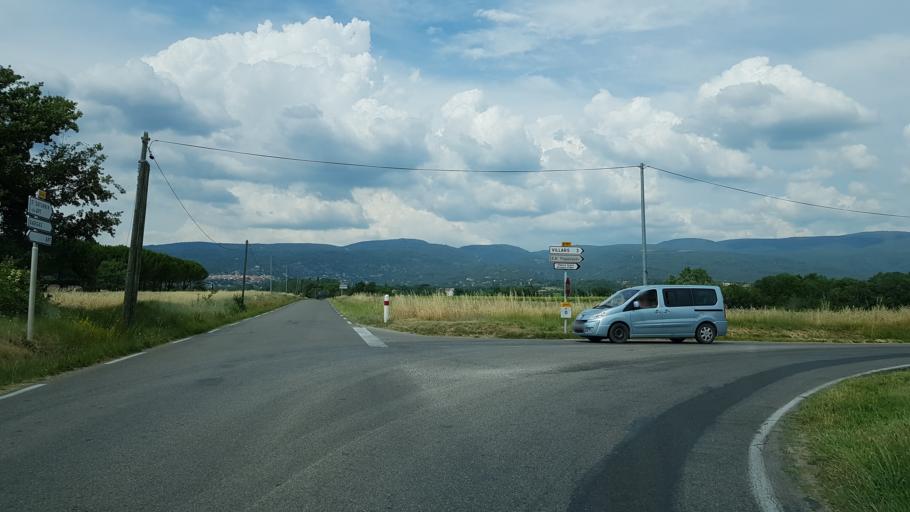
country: FR
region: Provence-Alpes-Cote d'Azur
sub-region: Departement du Vaucluse
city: Saint-Saturnin-les-Apt
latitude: 43.9113
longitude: 5.3838
